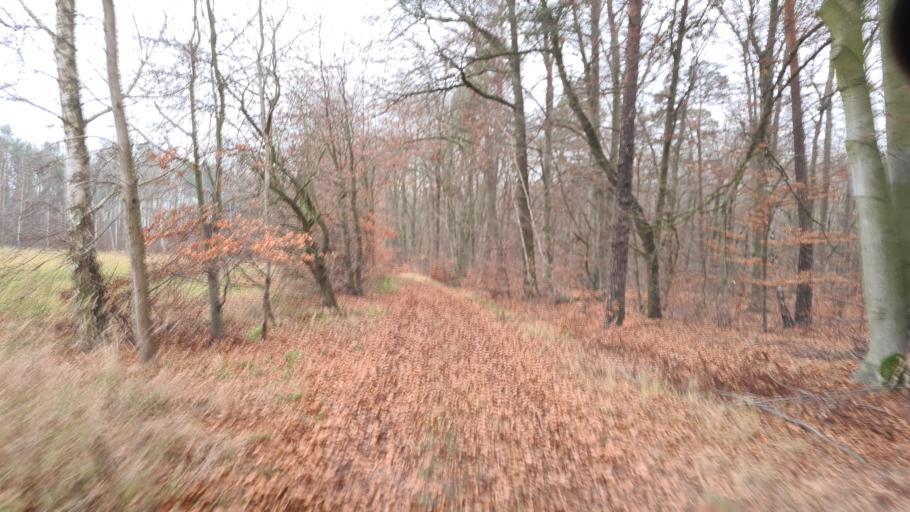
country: DE
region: Brandenburg
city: Doberlug-Kirchhain
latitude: 51.6295
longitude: 13.5296
